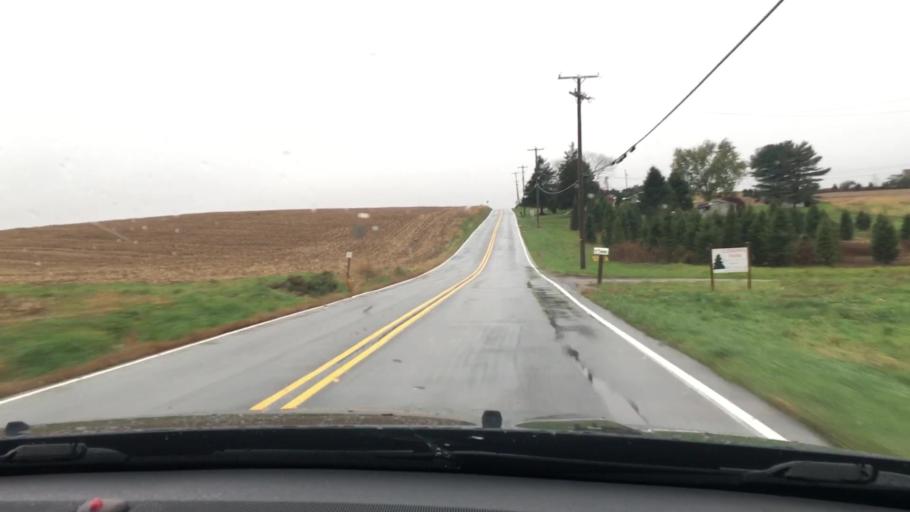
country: US
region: Pennsylvania
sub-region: York County
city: Susquehanna Trails
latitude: 39.7587
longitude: -76.4722
